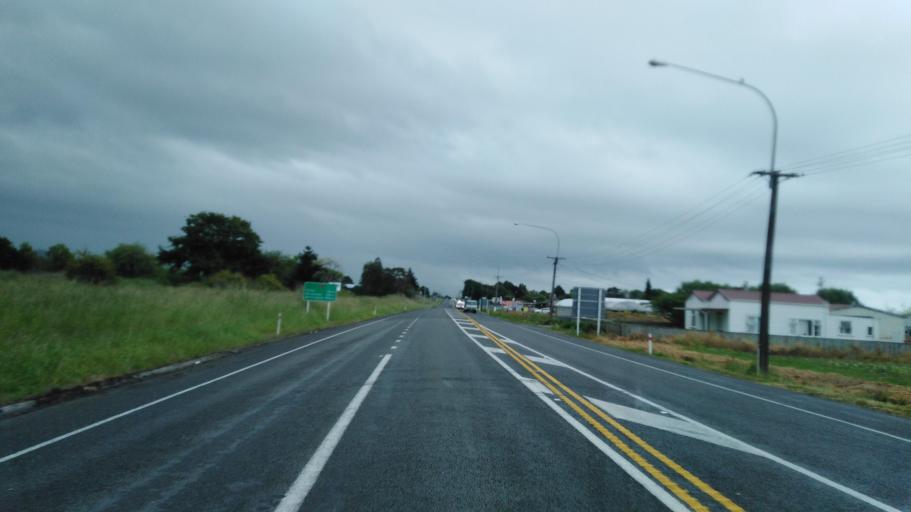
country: NZ
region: Manawatu-Wanganui
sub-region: Horowhenua District
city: Levin
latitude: -40.6495
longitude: 175.2589
